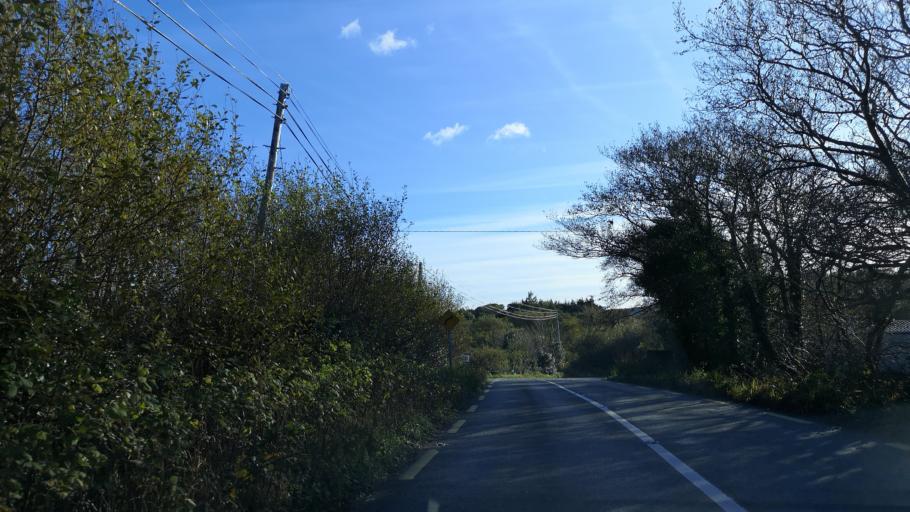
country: IE
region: Connaught
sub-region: County Galway
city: Clifden
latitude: 53.5455
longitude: -9.9741
